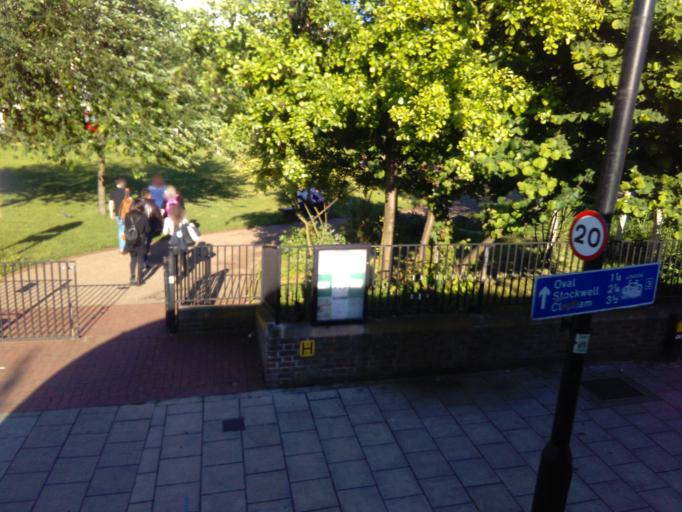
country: GB
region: England
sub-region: Greater London
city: Lambeth
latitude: 51.5016
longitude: -0.1104
